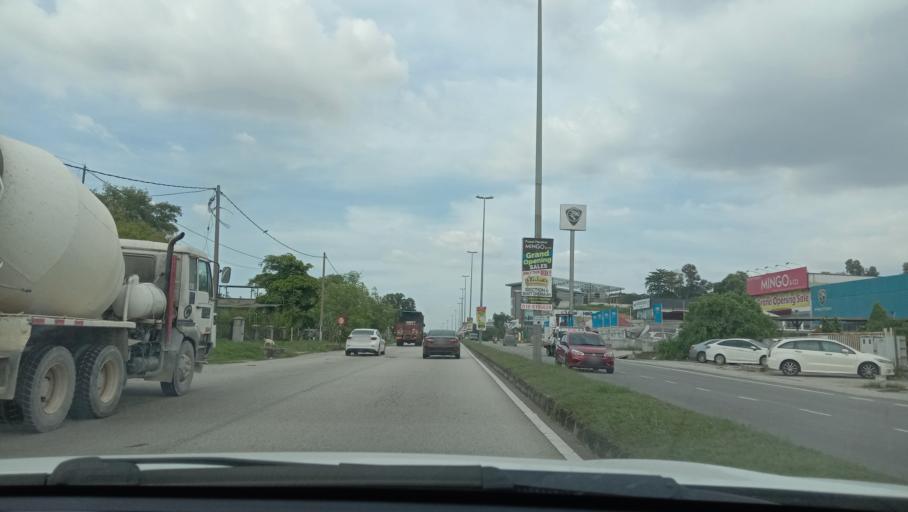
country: MY
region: Selangor
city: Kampung Baru Subang
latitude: 3.1326
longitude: 101.5259
